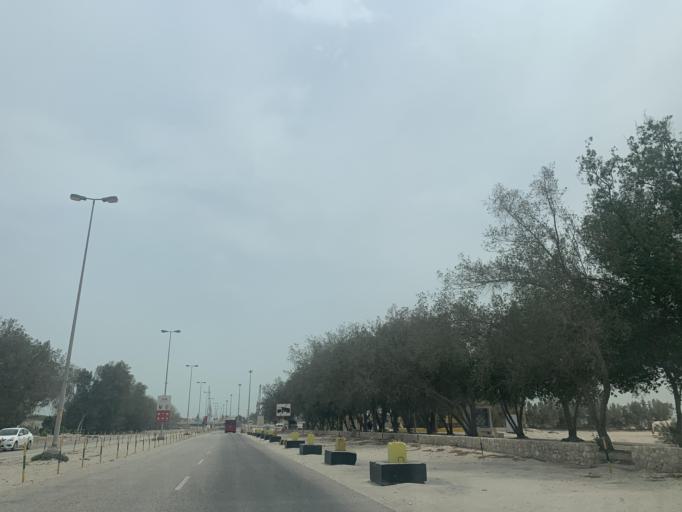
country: BH
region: Muharraq
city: Al Hadd
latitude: 26.1973
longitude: 50.6628
